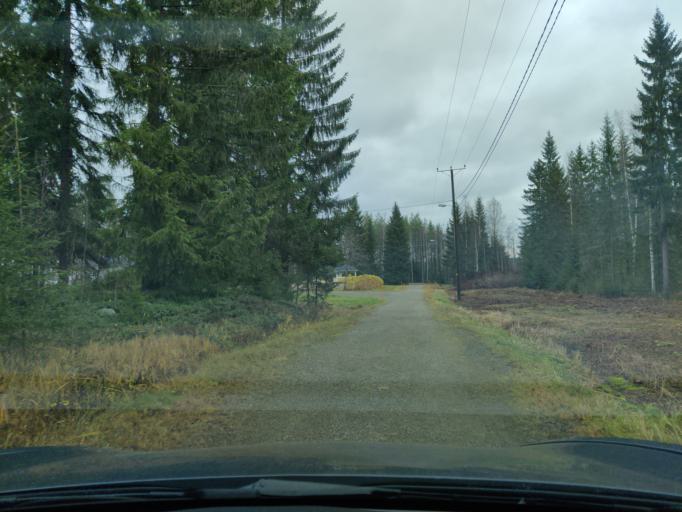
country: FI
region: Northern Savo
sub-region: Ylae-Savo
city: Kiuruvesi
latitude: 63.6409
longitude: 26.6394
